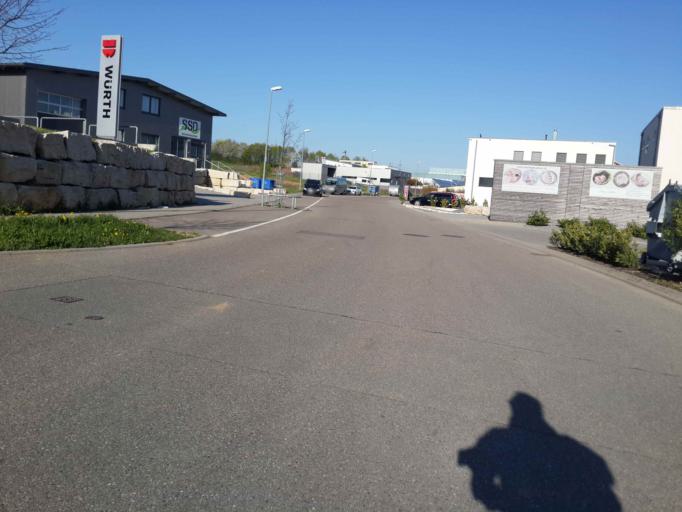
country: DE
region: Baden-Wuerttemberg
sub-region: Regierungsbezirk Stuttgart
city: Leingarten
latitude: 49.1508
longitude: 9.1222
